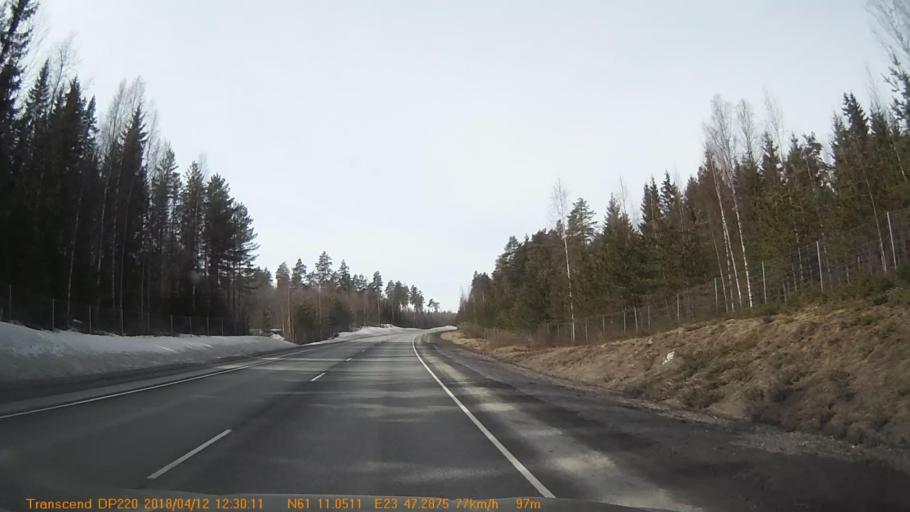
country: FI
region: Pirkanmaa
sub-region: Etelae-Pirkanmaa
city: Viiala
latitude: 61.1841
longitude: 23.7874
